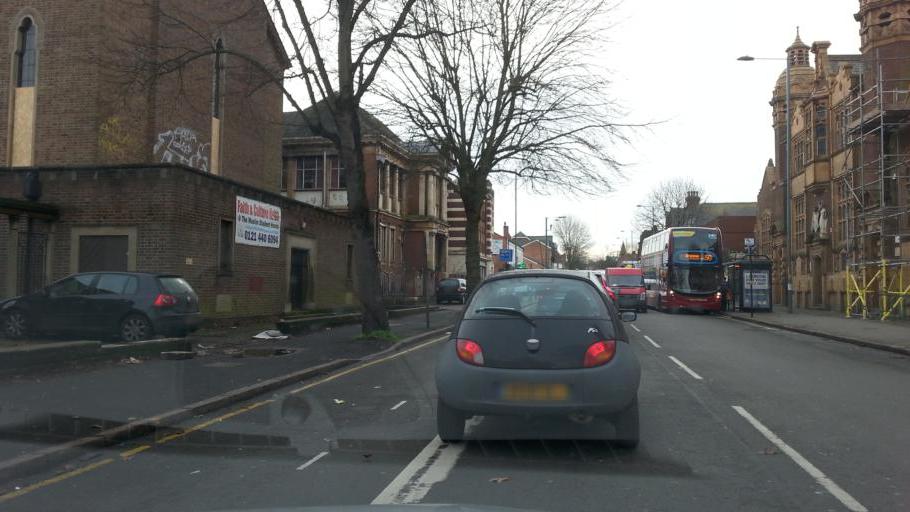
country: GB
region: England
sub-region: City and Borough of Birmingham
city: Birmingham
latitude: 52.4578
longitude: -1.8855
